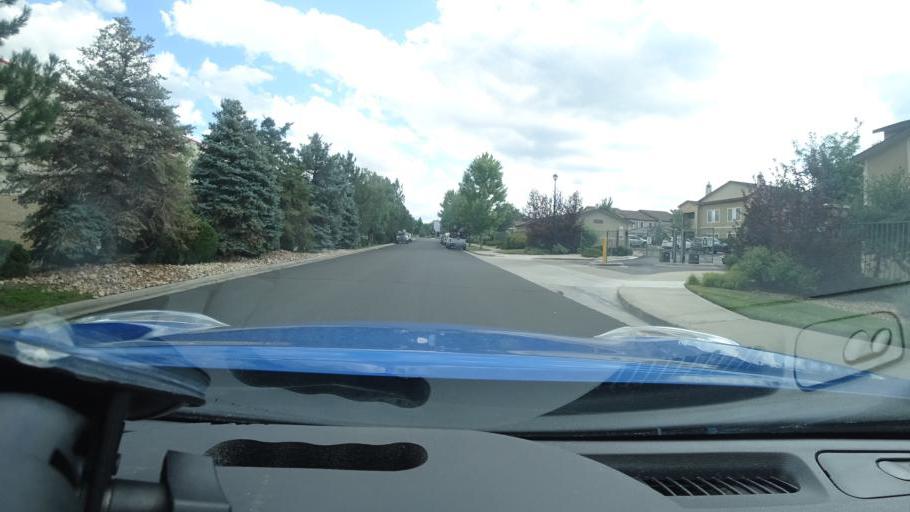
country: US
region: Colorado
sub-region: Adams County
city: Aurora
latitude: 39.6908
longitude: -104.8695
